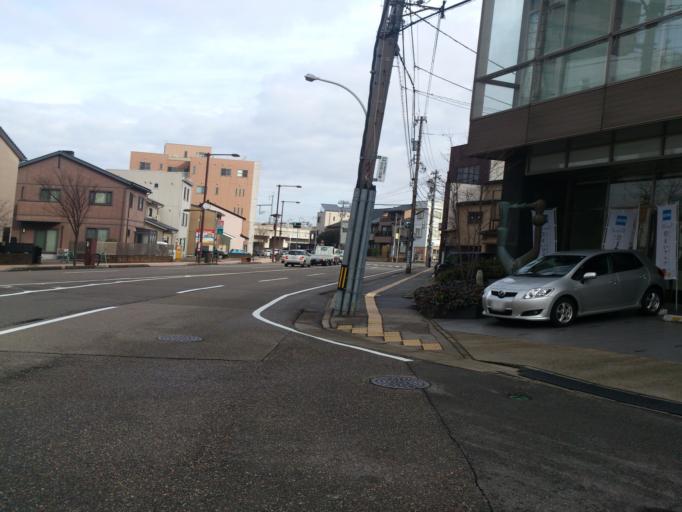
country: JP
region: Ishikawa
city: Kanazawa-shi
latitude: 36.5808
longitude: 136.6522
